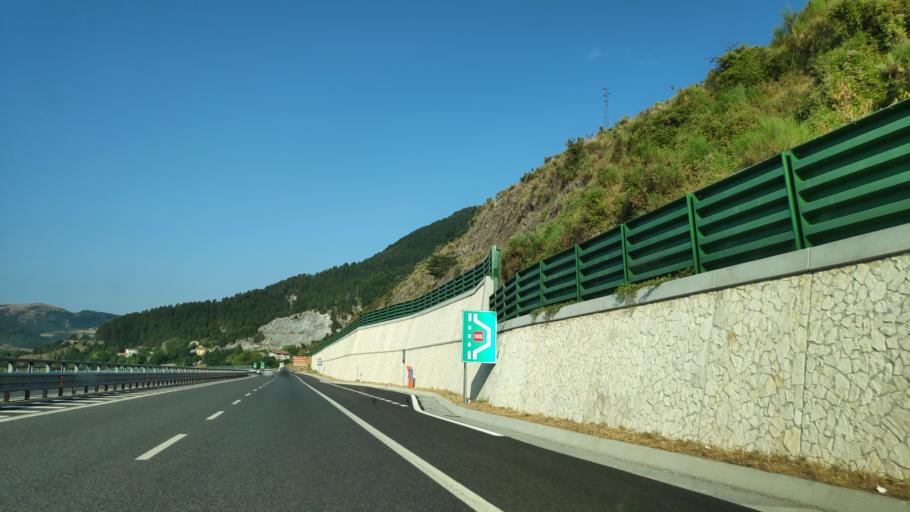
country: IT
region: Calabria
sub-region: Provincia di Cosenza
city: Mormanno
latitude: 39.8846
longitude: 16.0173
